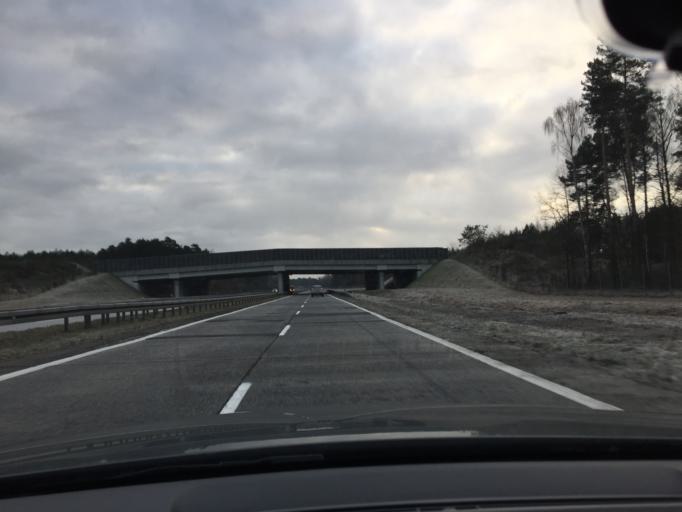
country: PL
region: Lubusz
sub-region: Powiat zarski
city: Lipinki Luzyckie
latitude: 51.6021
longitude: 14.9900
